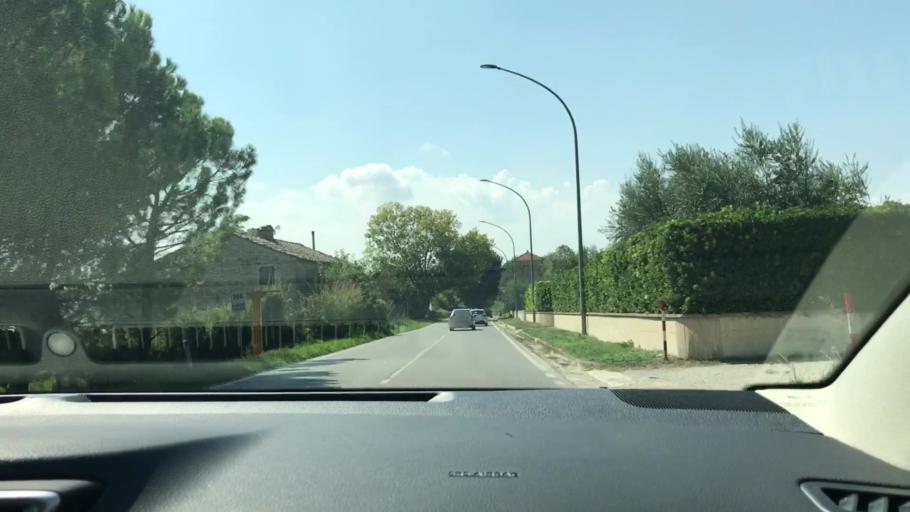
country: IT
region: The Marches
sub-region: Provincia di Ascoli Piceno
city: San Benedetto del Tronto
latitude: 42.9048
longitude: 13.8659
